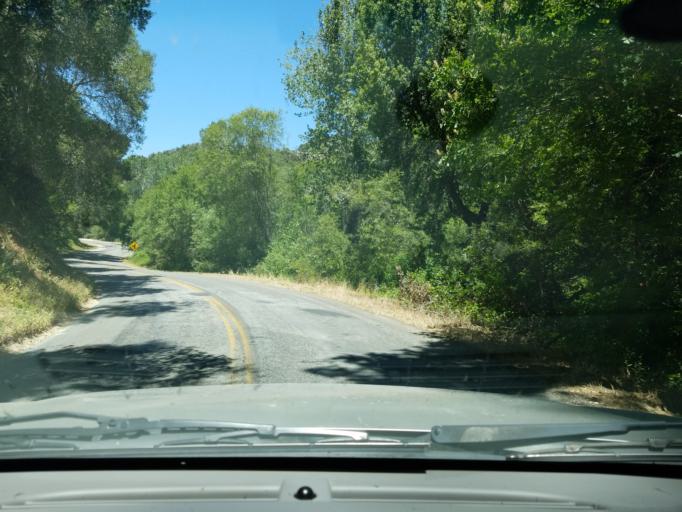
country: US
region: California
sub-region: Monterey County
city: Carmel Valley Village
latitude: 36.4453
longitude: -121.6799
